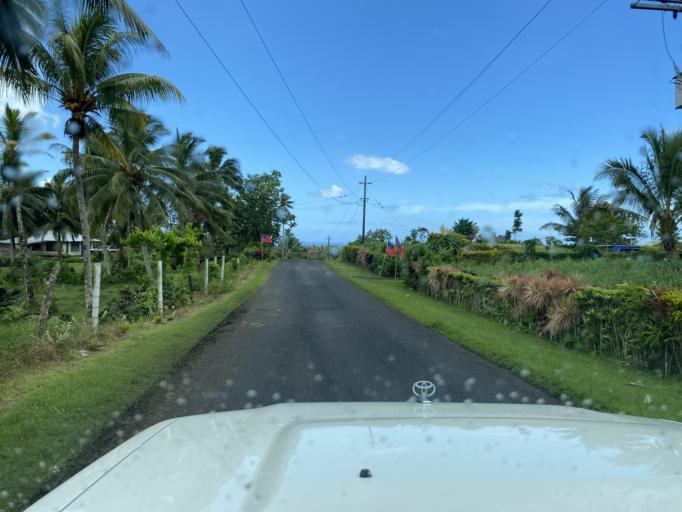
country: WS
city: Matavai
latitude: -13.9903
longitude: -171.5860
